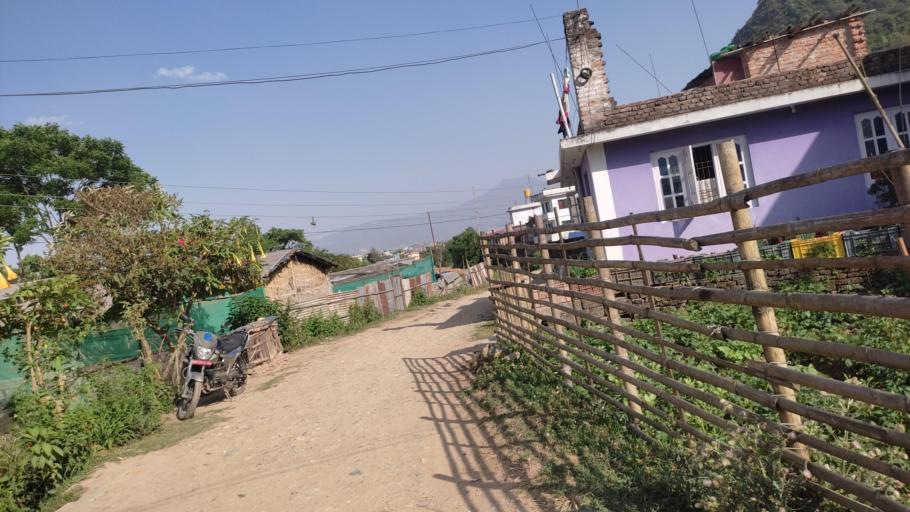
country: NP
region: Central Region
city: Kirtipur
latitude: 27.6603
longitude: 85.2630
